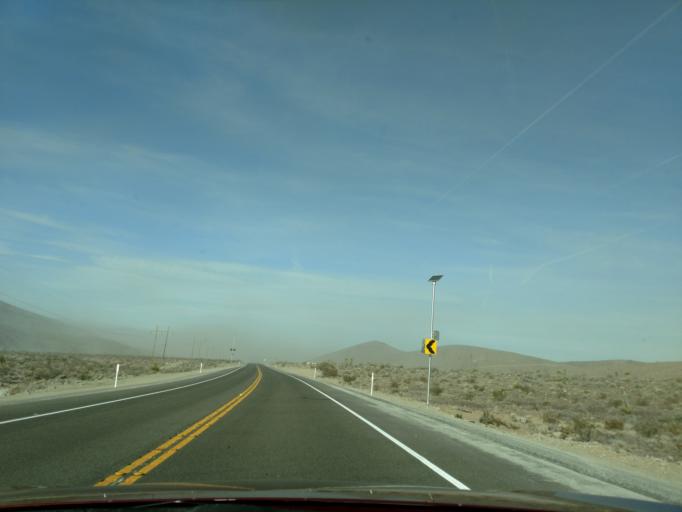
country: US
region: Nevada
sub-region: Nye County
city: Pahrump
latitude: 36.4361
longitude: -116.0764
